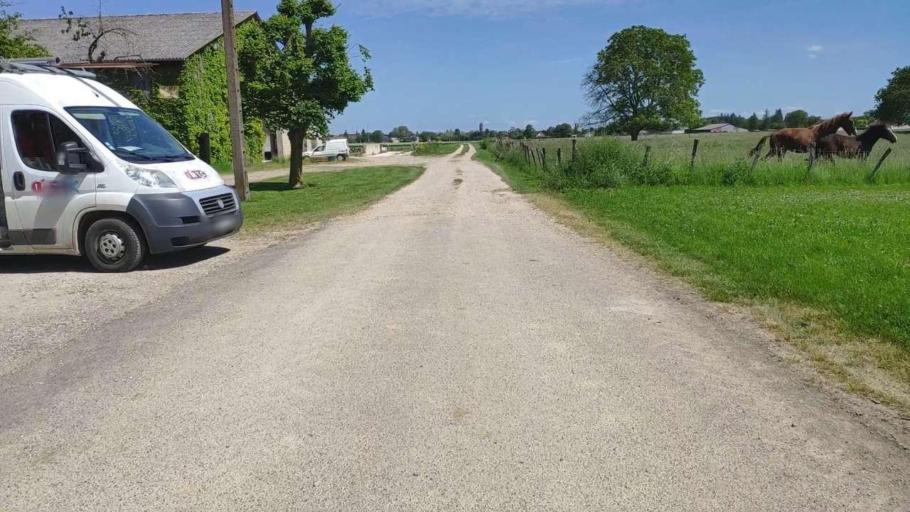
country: FR
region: Franche-Comte
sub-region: Departement du Jura
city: Bletterans
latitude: 46.7336
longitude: 5.4555
